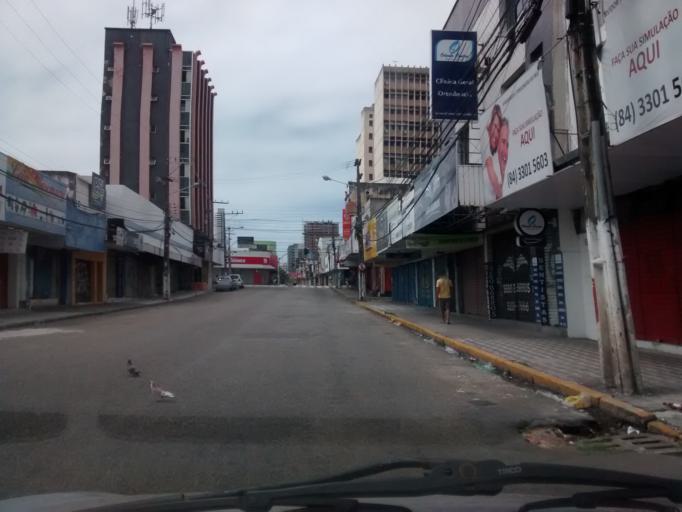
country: BR
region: Rio Grande do Norte
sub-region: Natal
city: Natal
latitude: -5.7847
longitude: -35.2072
